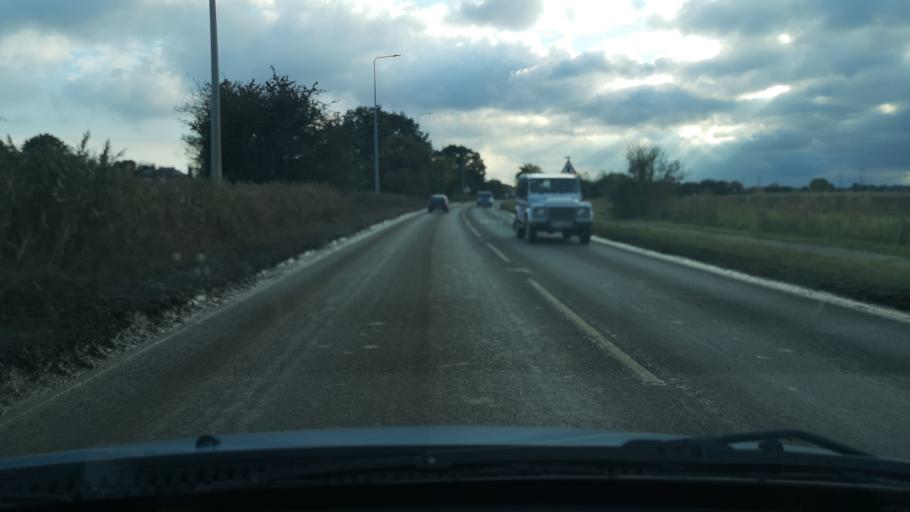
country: GB
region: England
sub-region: North Lincolnshire
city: Gunness
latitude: 53.5816
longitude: -0.7387
